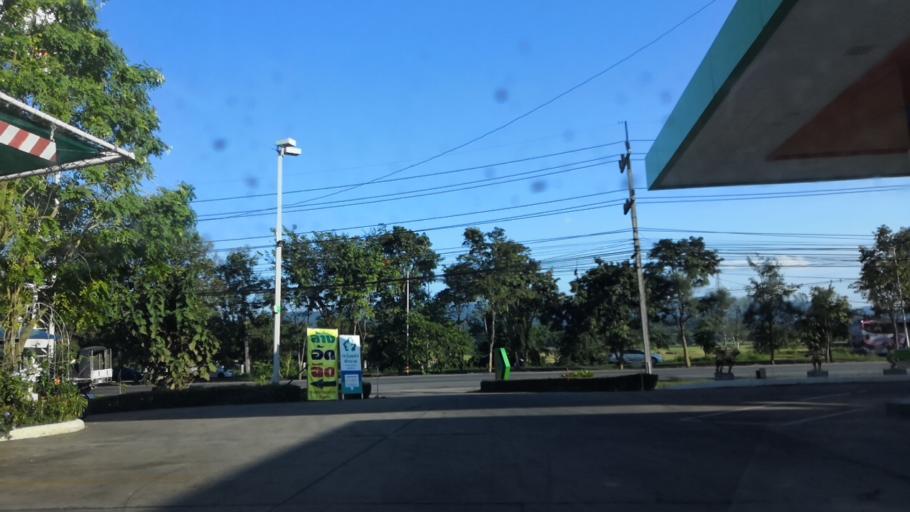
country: TH
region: Chiang Rai
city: Mae Lao
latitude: 19.7546
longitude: 99.7313
